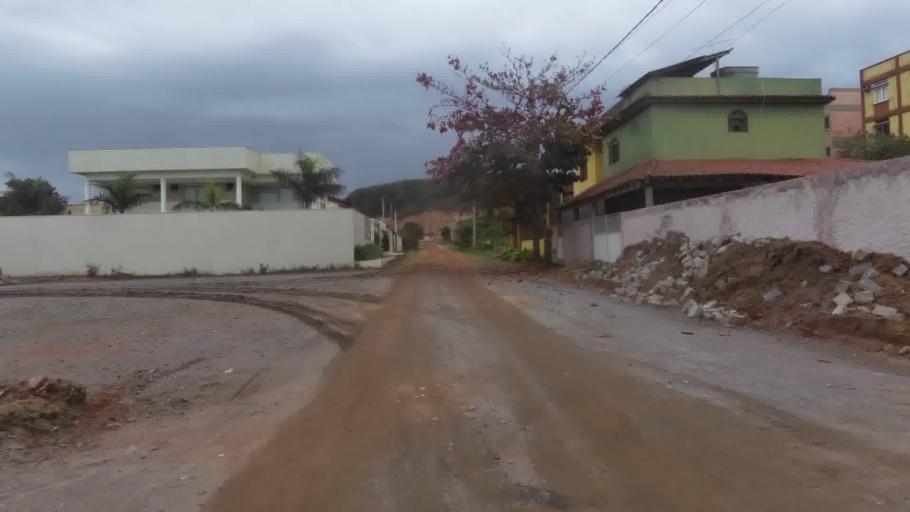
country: BR
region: Espirito Santo
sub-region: Marataizes
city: Marataizes
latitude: -21.0567
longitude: -40.8337
